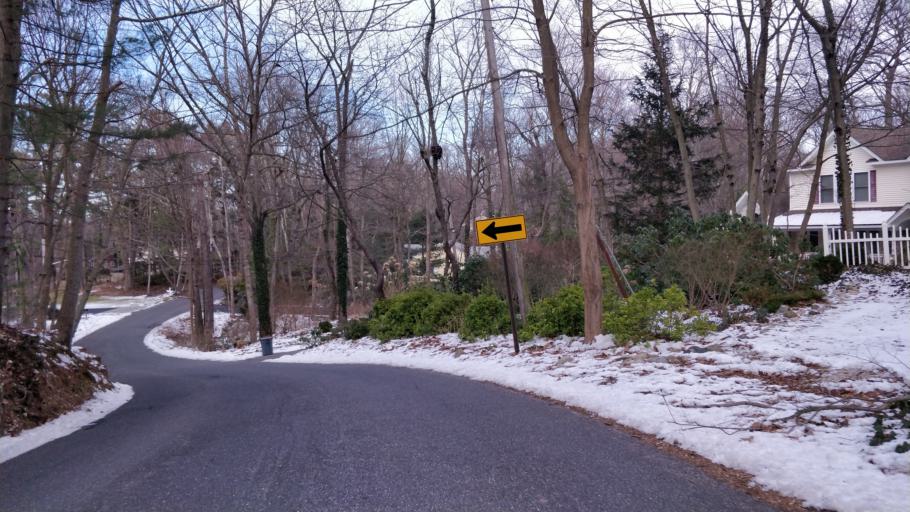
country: US
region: New York
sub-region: Suffolk County
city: Northport
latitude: 40.8834
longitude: -73.3450
